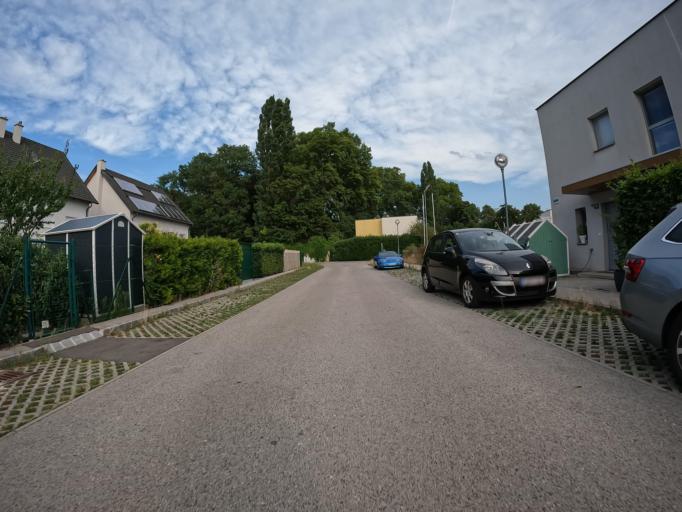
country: AT
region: Lower Austria
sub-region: Politischer Bezirk Baden
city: Traiskirchen
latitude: 48.0183
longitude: 16.3002
